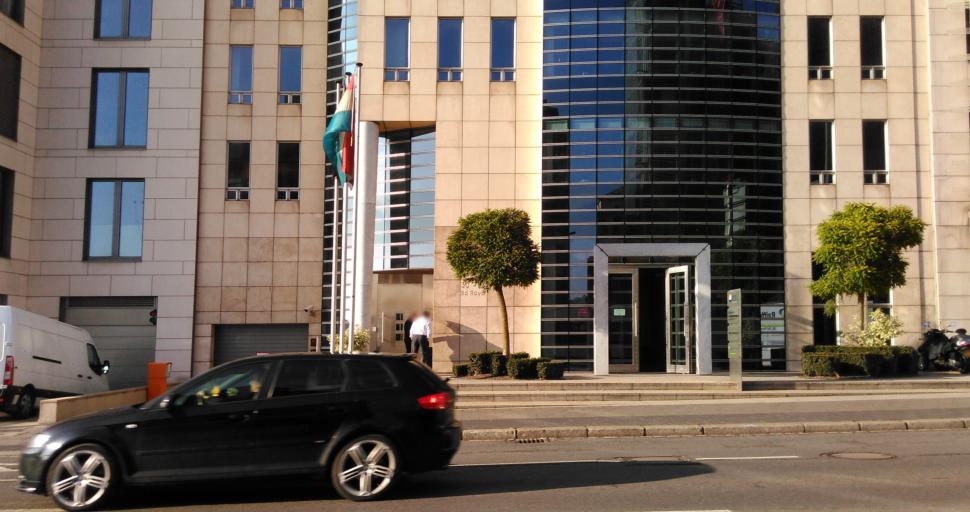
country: LU
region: Luxembourg
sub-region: Canton de Luxembourg
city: Luxembourg
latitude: 49.6098
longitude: 6.1262
